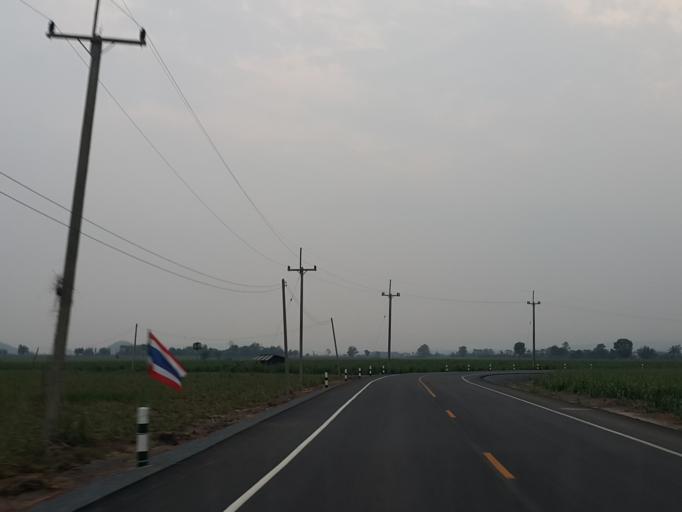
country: TH
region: Suphan Buri
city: Dan Chang
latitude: 14.9446
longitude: 99.6569
